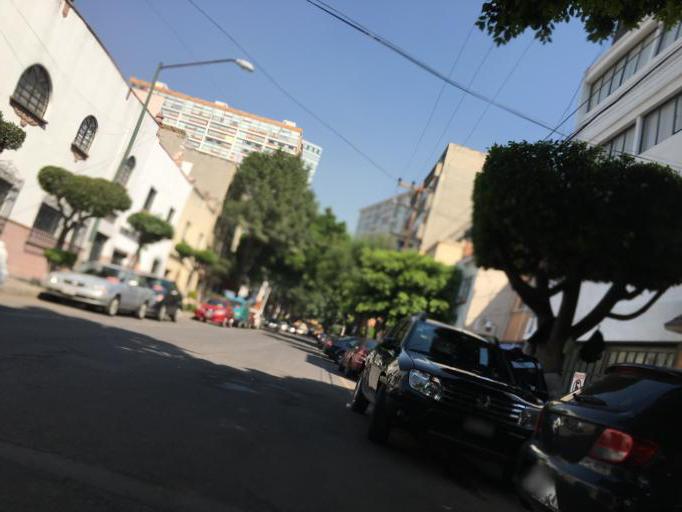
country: MX
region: Mexico City
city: Miguel Hidalgo
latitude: 19.4362
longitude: -99.1772
